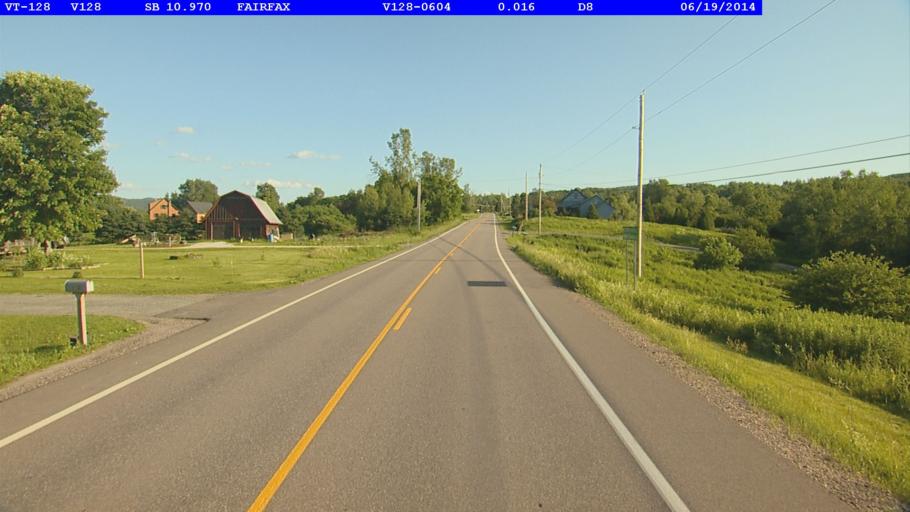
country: US
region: Vermont
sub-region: Chittenden County
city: Milton
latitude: 44.6475
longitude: -73.0141
